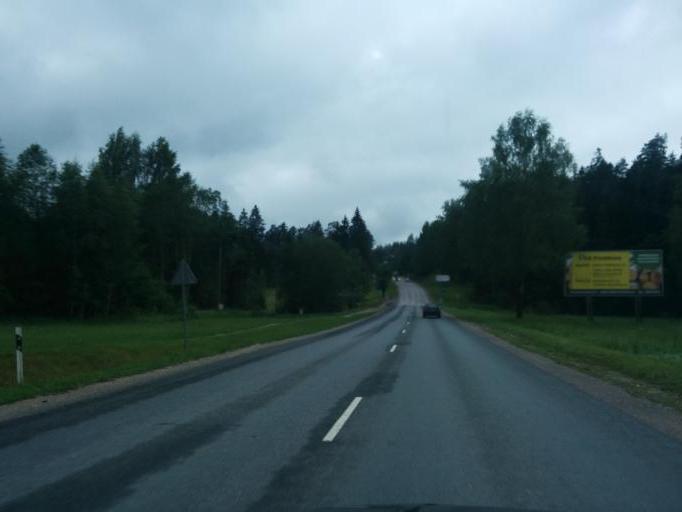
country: LV
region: Smiltene
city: Smiltene
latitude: 57.4172
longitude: 25.9293
